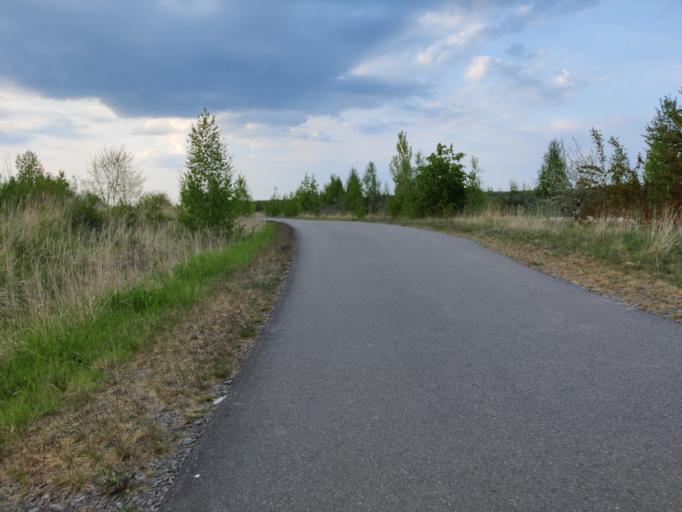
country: DE
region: Saxony
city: Rotha
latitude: 51.2397
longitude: 12.4406
